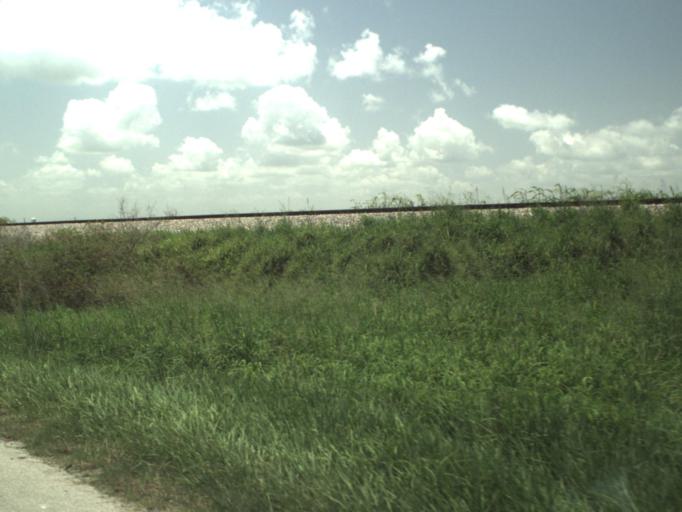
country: US
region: Florida
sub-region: Palm Beach County
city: Pahokee
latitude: 26.8325
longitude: -80.6445
